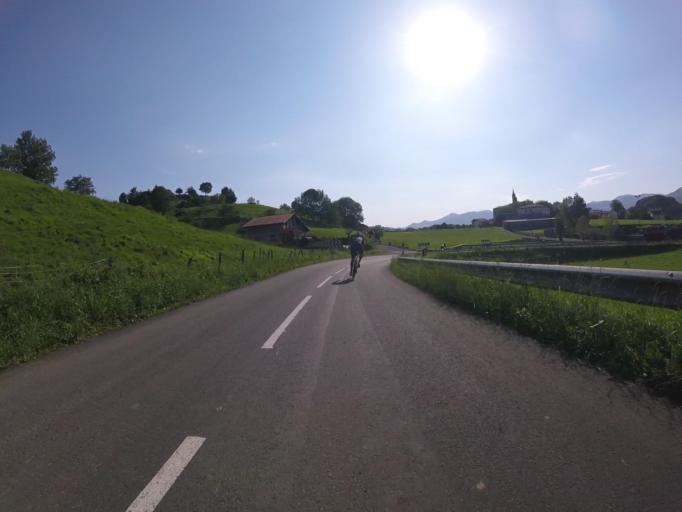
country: ES
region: Basque Country
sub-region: Provincia de Guipuzcoa
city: Asteasu
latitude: 43.1977
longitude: -2.1003
